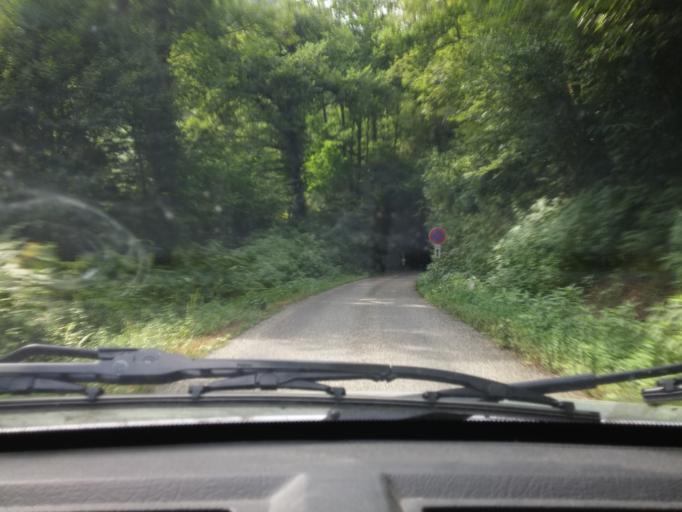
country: FR
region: Midi-Pyrenees
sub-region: Departement de l'Ariege
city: Saint-Girons
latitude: 42.9142
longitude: 1.1935
